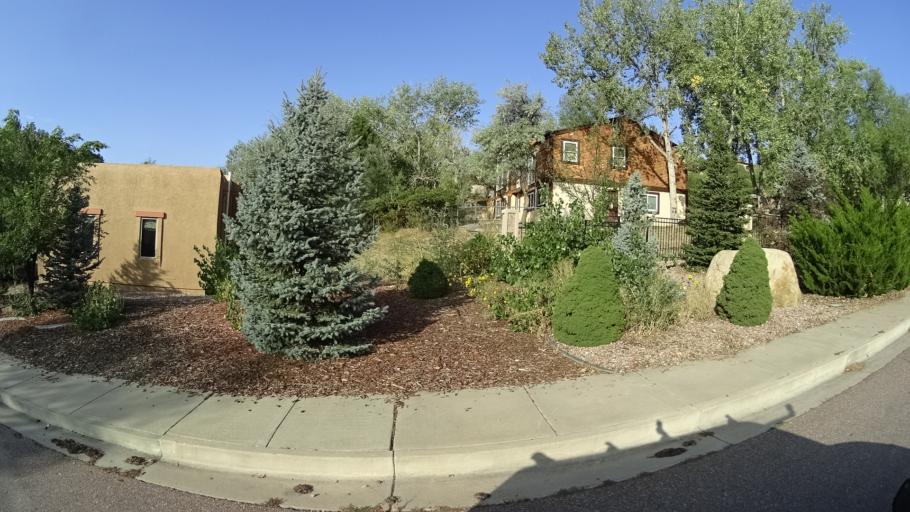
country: US
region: Colorado
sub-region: El Paso County
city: Colorado Springs
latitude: 38.8134
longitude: -104.8539
